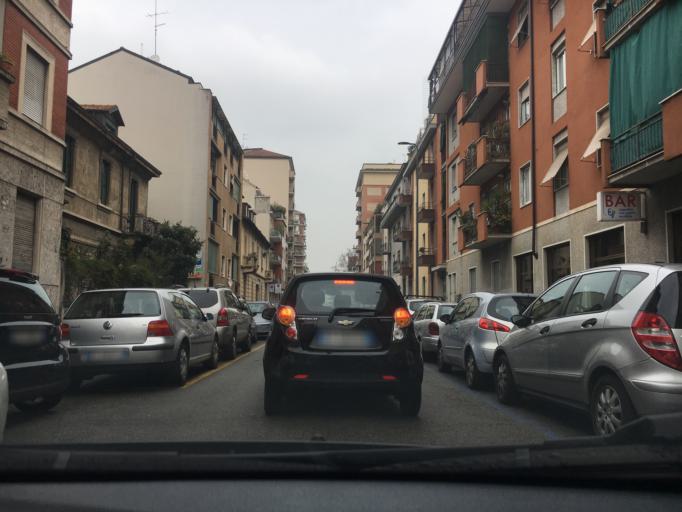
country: IT
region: Lombardy
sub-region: Citta metropolitana di Milano
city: Romano Banco
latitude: 45.4680
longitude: 9.1437
